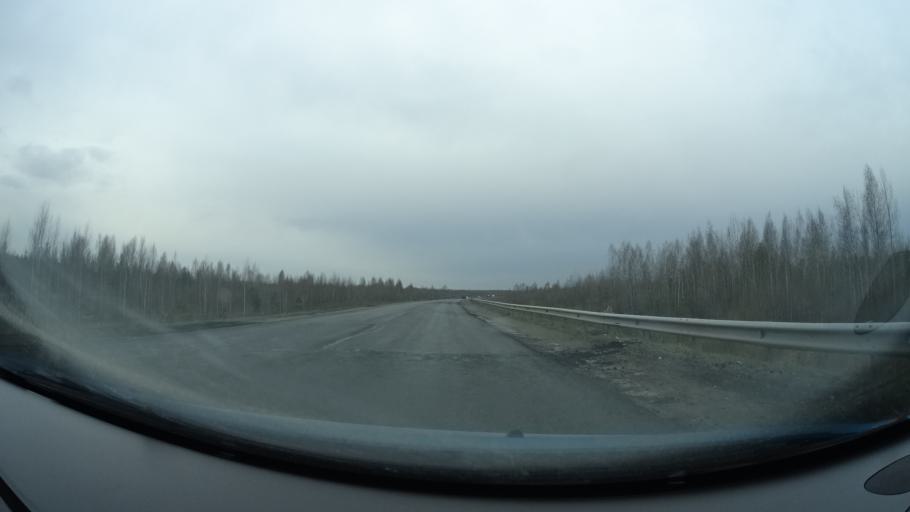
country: RU
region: Perm
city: Krasnokamsk
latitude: 58.0921
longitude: 55.7293
